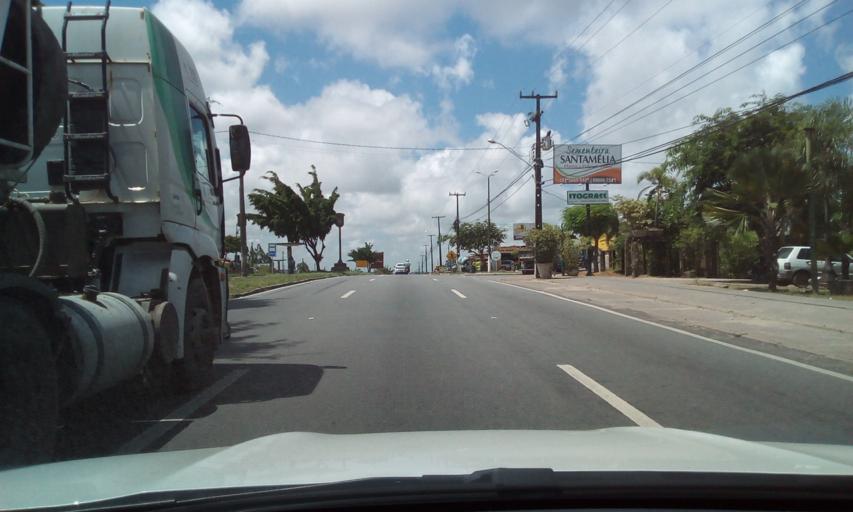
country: BR
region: Pernambuco
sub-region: Igarassu
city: Igarassu
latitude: -7.8430
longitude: -34.9109
